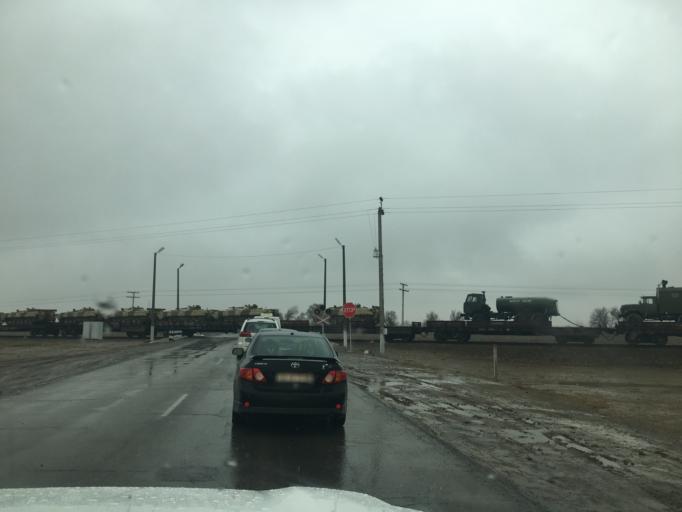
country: TM
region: Mary
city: Yoloeten
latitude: 37.3901
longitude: 62.1812
